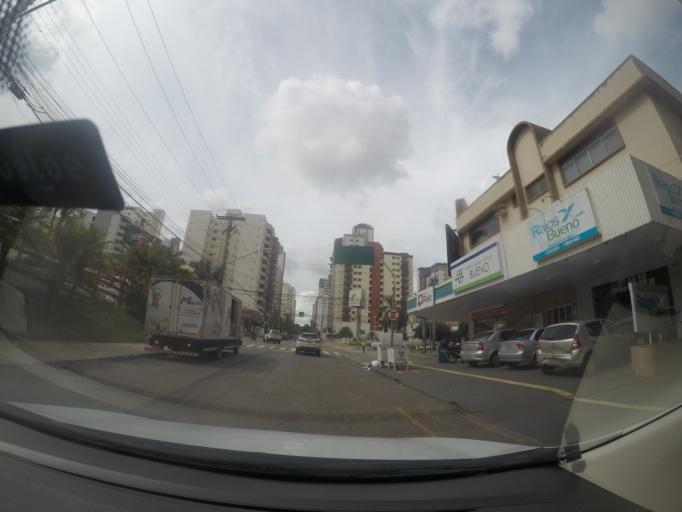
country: BR
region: Goias
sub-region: Goiania
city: Goiania
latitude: -16.7138
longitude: -49.2691
